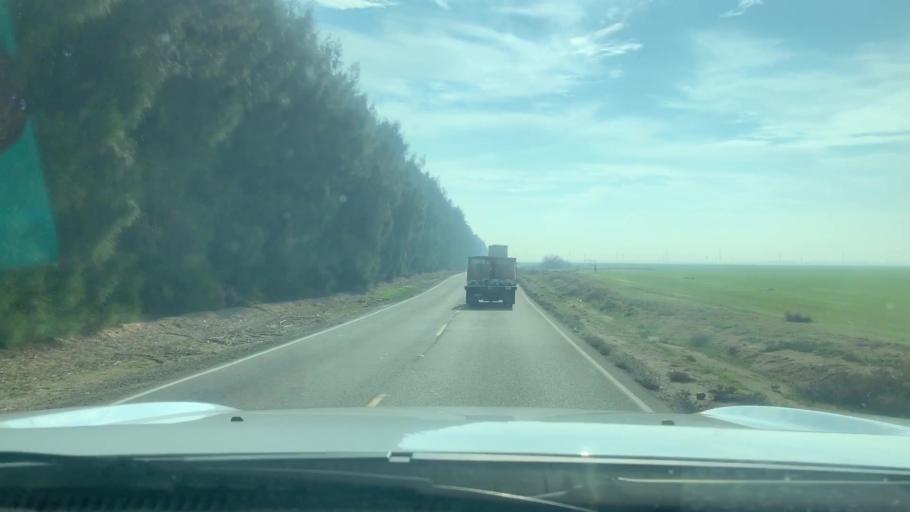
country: US
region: California
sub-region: Kern County
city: Lost Hills
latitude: 35.5092
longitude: -119.7470
